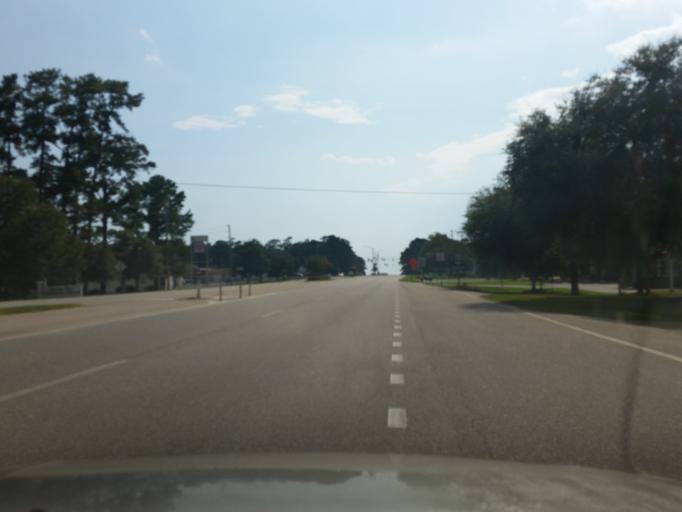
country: US
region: Alabama
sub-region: Baldwin County
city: Spanish Fort
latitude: 30.6696
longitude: -87.9082
